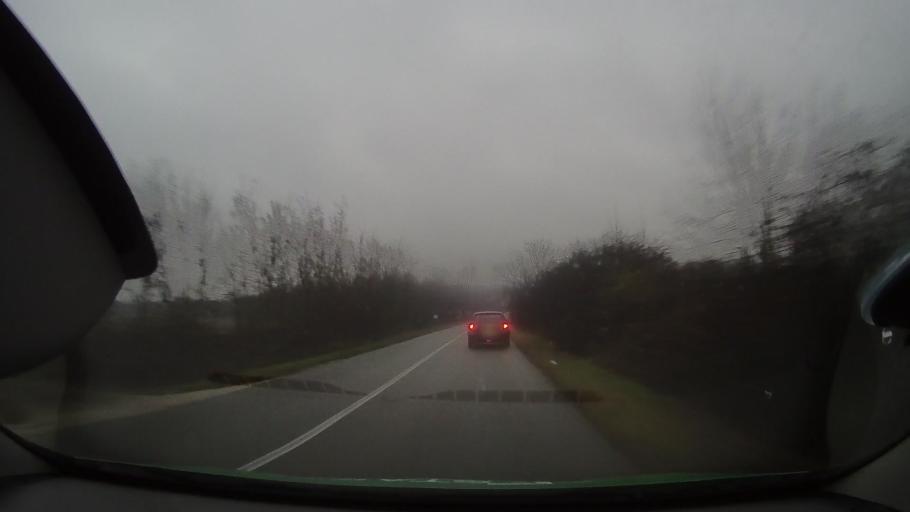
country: RO
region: Arad
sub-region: Comuna Craiova
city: Craiova
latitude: 46.5940
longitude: 21.9777
